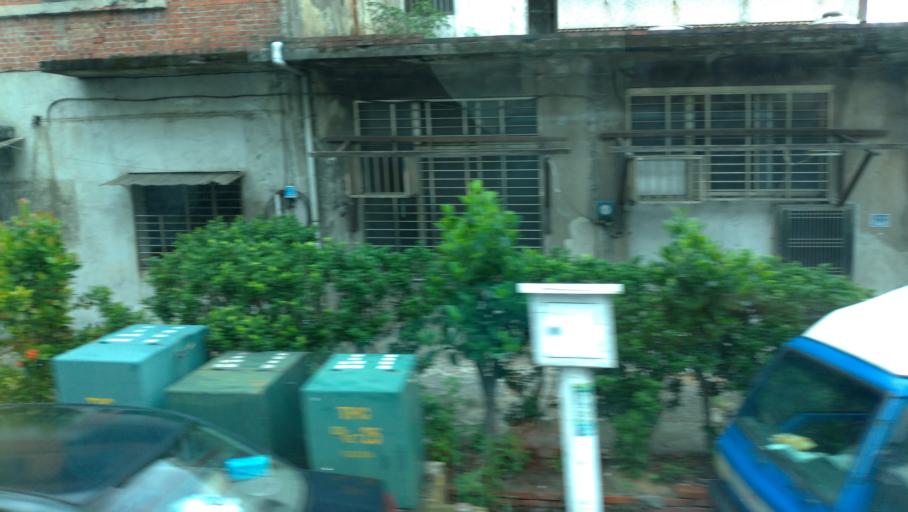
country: TW
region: Taiwan
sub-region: Keelung
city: Keelung
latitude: 25.1520
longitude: 121.7679
